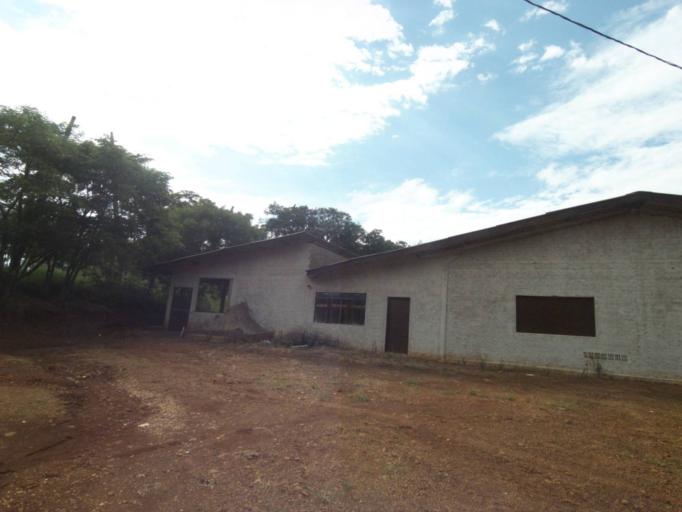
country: BR
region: Parana
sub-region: Pitanga
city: Pitanga
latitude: -24.9093
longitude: -52.0339
